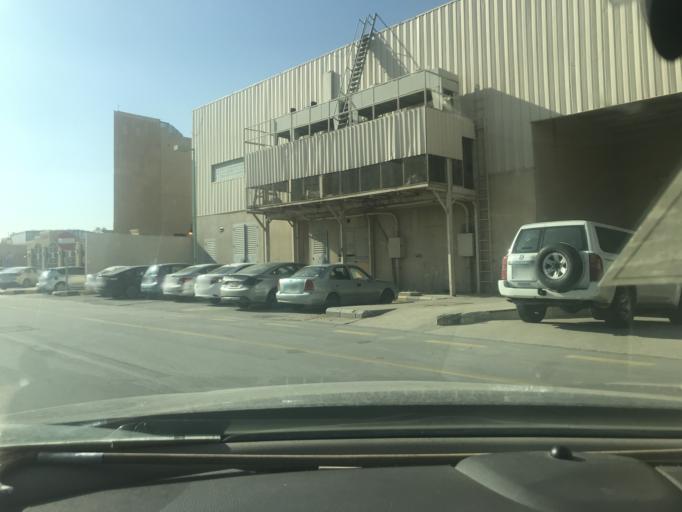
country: SA
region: Ar Riyad
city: Riyadh
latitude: 24.7538
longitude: 46.6663
